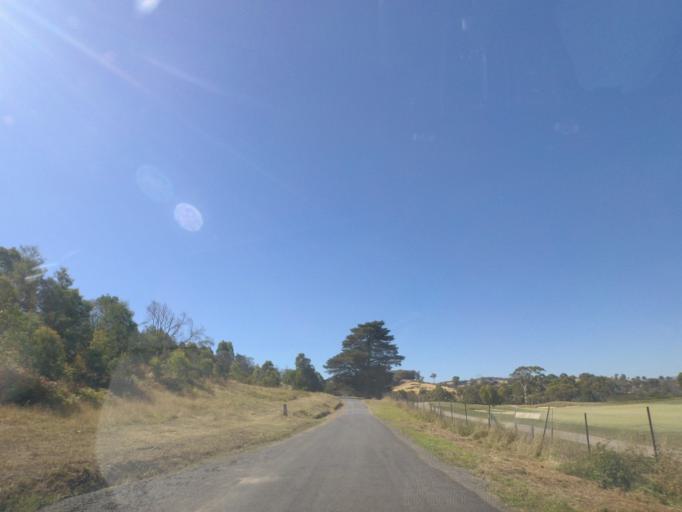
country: AU
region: Victoria
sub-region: Yarra Ranges
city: Chirnside Park
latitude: -37.7166
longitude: 145.2929
